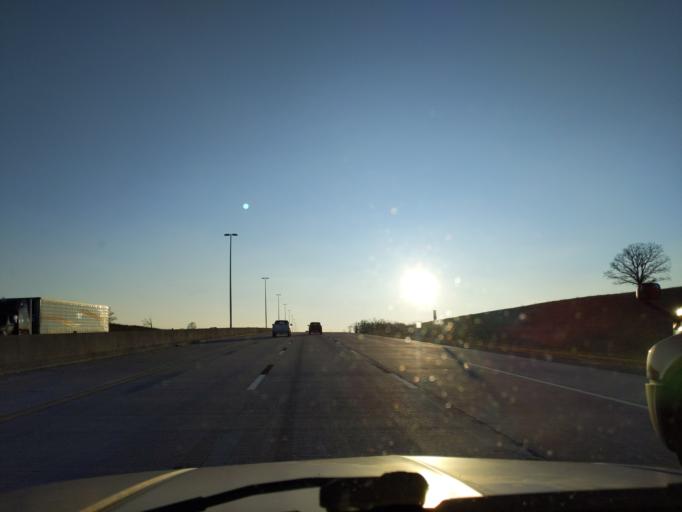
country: US
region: Oklahoma
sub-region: Creek County
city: Kellyville
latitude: 35.9424
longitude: -96.2563
